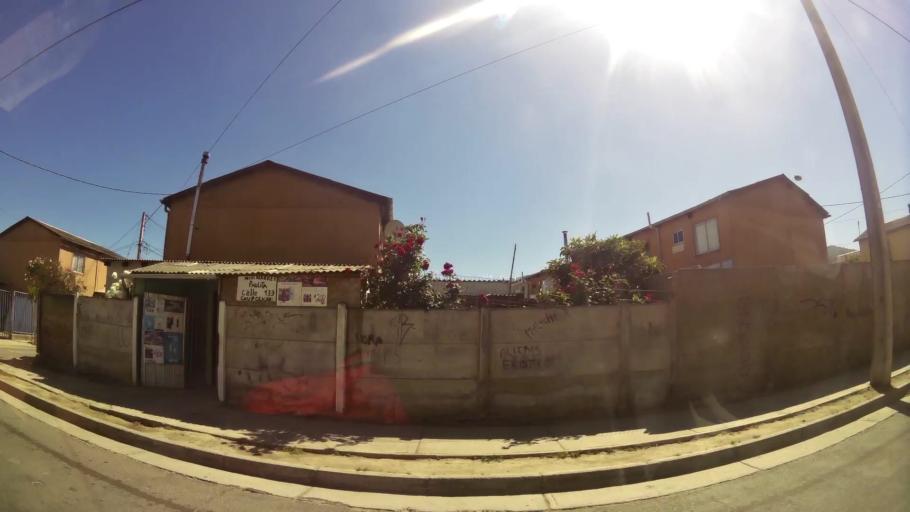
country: CL
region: Valparaiso
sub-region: Provincia de Marga Marga
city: Quilpue
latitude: -33.3157
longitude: -71.4067
